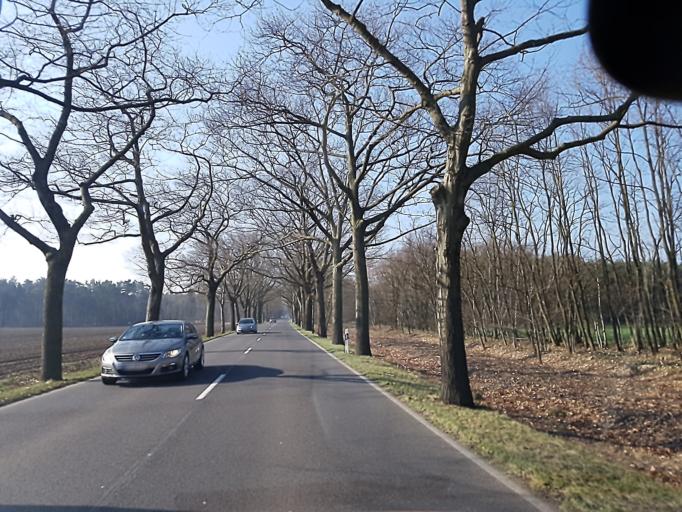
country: DE
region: Brandenburg
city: Forst
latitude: 51.6704
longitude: 14.5945
